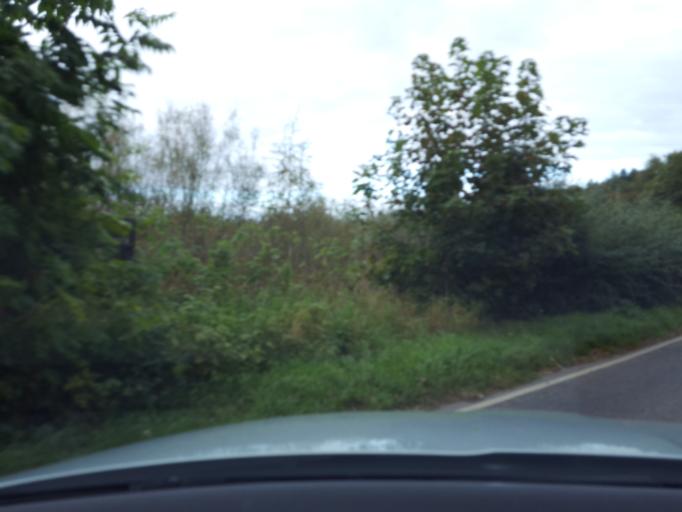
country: GB
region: Scotland
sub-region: Fife
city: Pathhead
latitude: 55.8570
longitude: -3.0007
